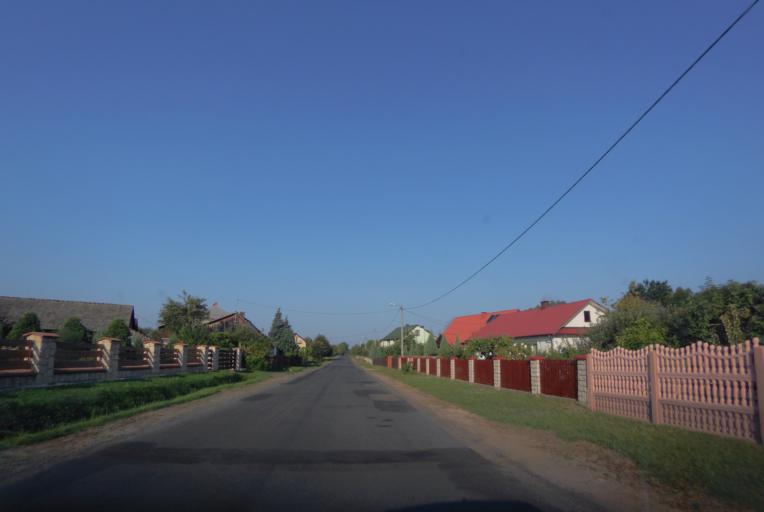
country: PL
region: Subcarpathian Voivodeship
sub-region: Powiat nizanski
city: Harasiuki
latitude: 50.5443
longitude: 22.5546
